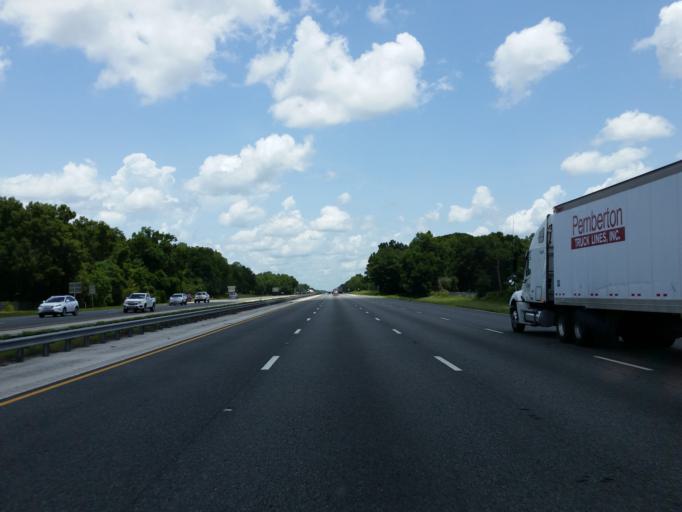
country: US
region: Florida
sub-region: Marion County
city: Ocala
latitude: 29.2714
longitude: -82.1946
